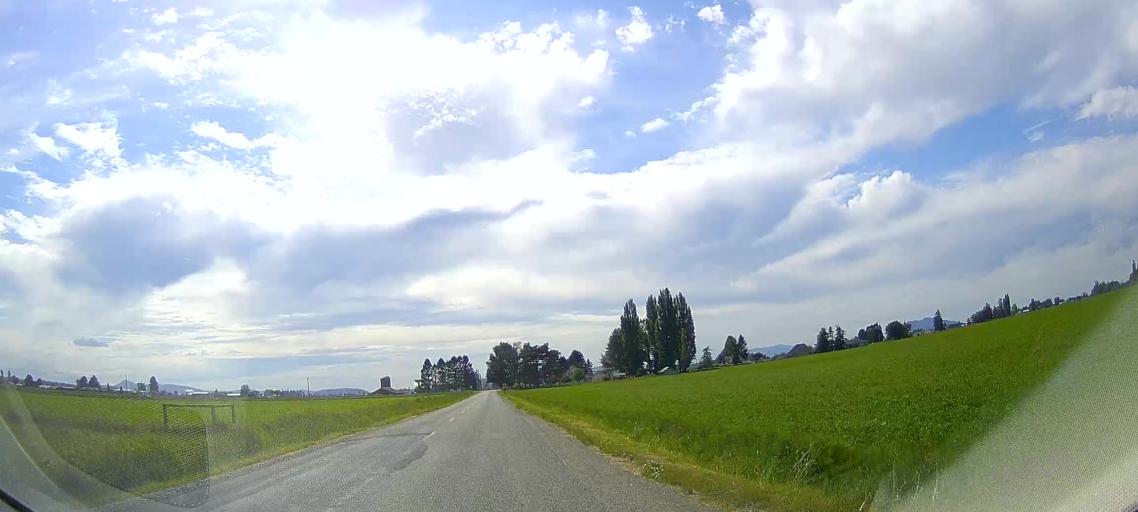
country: US
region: Washington
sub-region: Skagit County
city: Burlington
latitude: 48.5450
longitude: -122.4011
